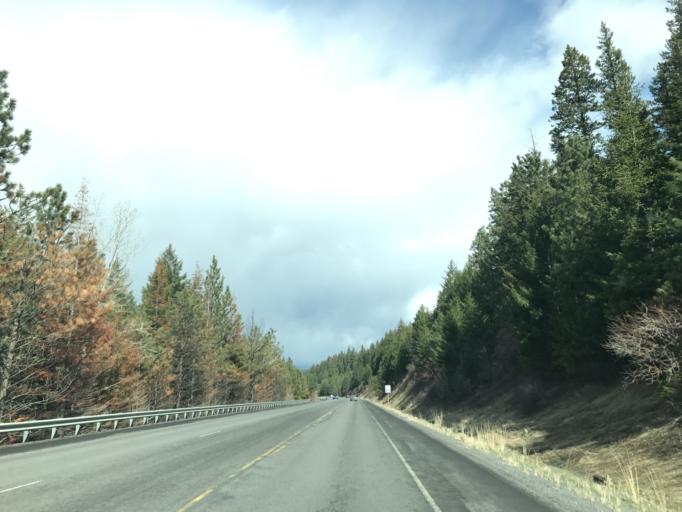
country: US
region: Idaho
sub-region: Idaho County
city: Grangeville
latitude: 45.8526
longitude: -116.2382
